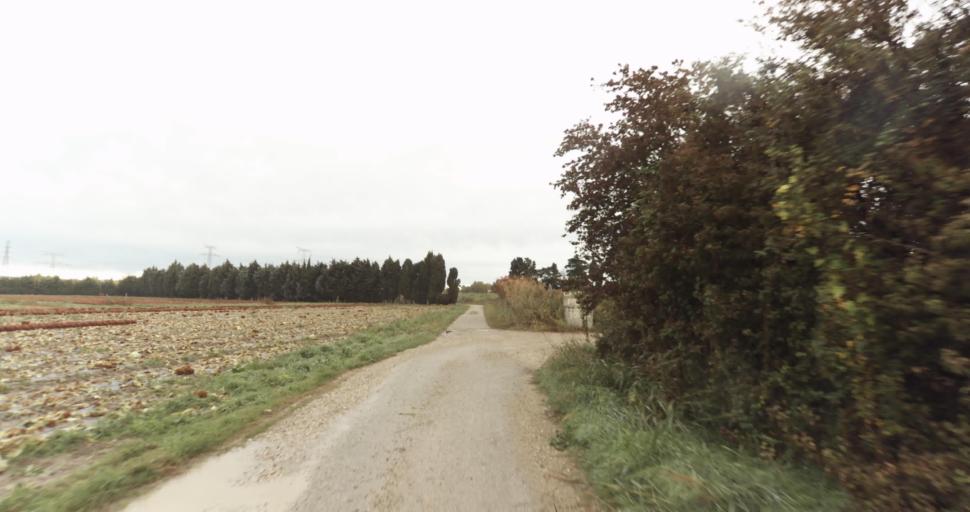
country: FR
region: Provence-Alpes-Cote d'Azur
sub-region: Departement des Bouches-du-Rhone
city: Rognonas
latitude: 43.9112
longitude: 4.7974
